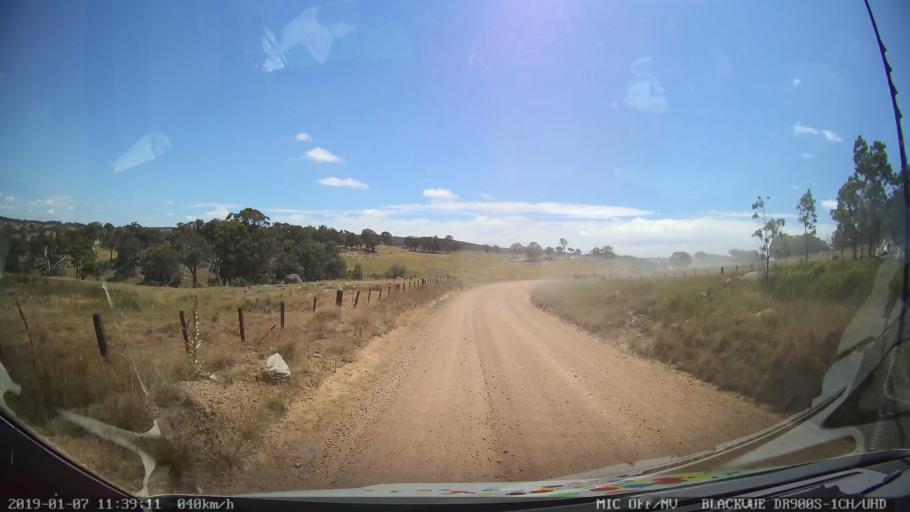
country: AU
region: New South Wales
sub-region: Armidale Dumaresq
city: Armidale
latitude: -30.3684
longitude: 151.5749
